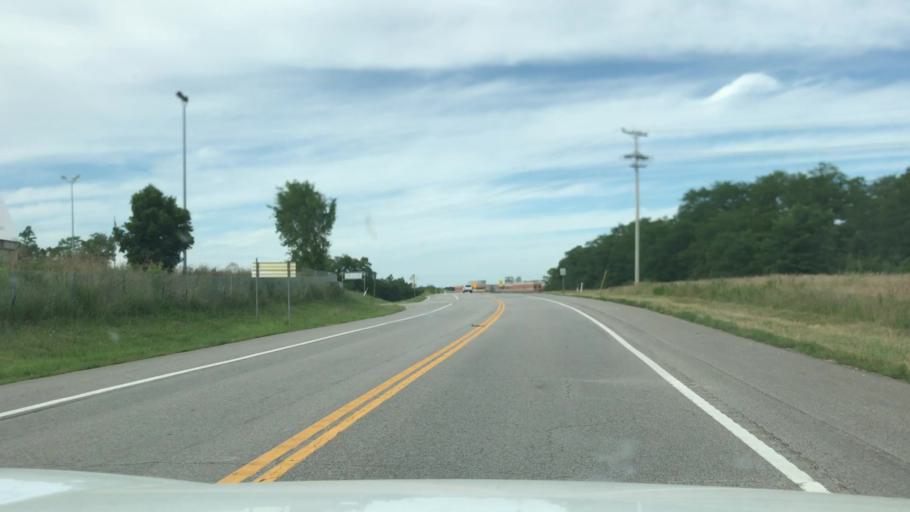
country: US
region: Missouri
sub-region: Saint Charles County
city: Weldon Spring
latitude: 38.6975
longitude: -90.7222
